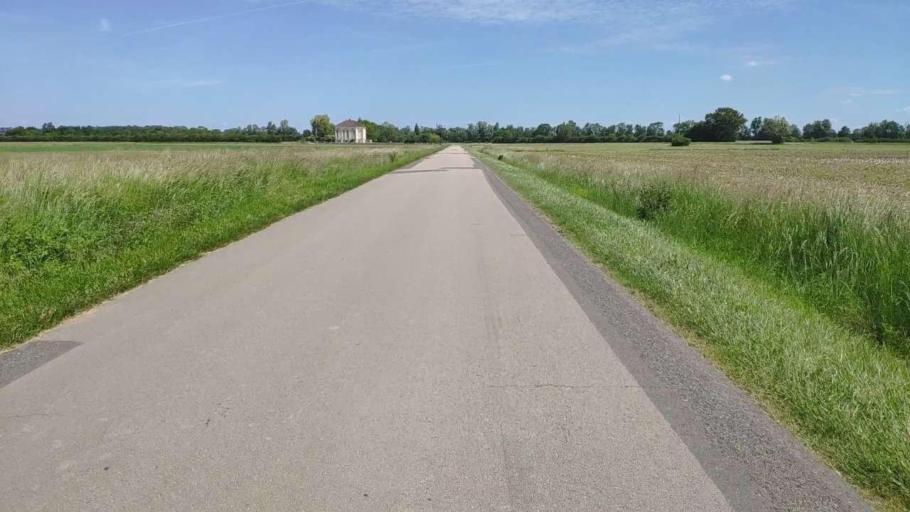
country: FR
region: Franche-Comte
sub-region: Departement du Jura
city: Bletterans
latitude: 46.7184
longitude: 5.4434
